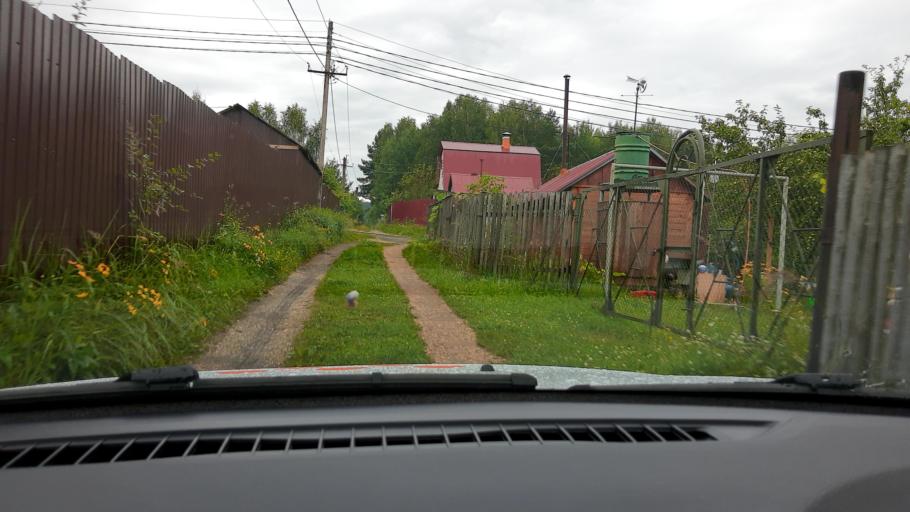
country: RU
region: Nizjnij Novgorod
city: Surovatikha
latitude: 55.9306
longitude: 43.9262
